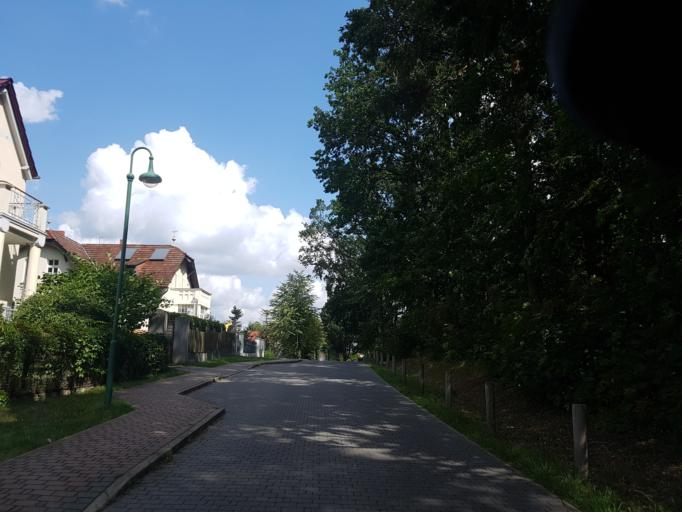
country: DE
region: Brandenburg
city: Gross Kreutz
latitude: 52.3106
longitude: 12.7384
